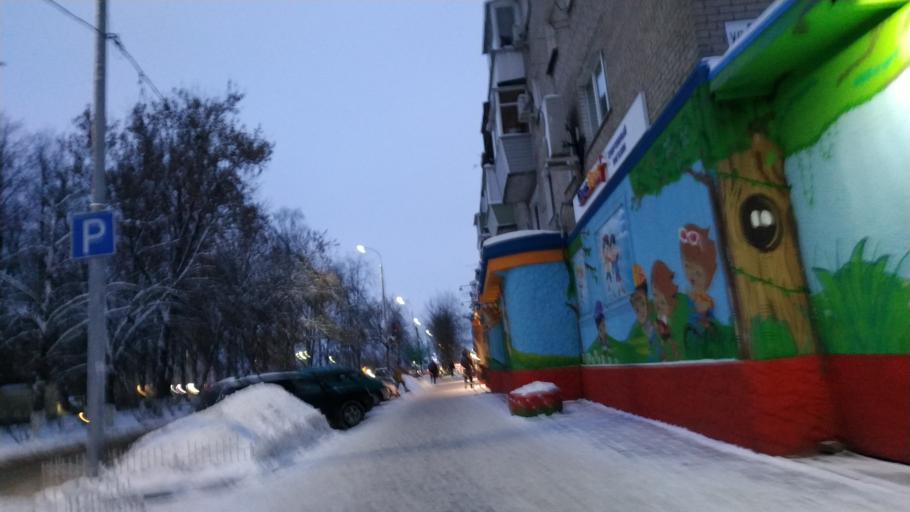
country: RU
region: Moskovskaya
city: Shchelkovo
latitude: 55.9208
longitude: 37.9753
